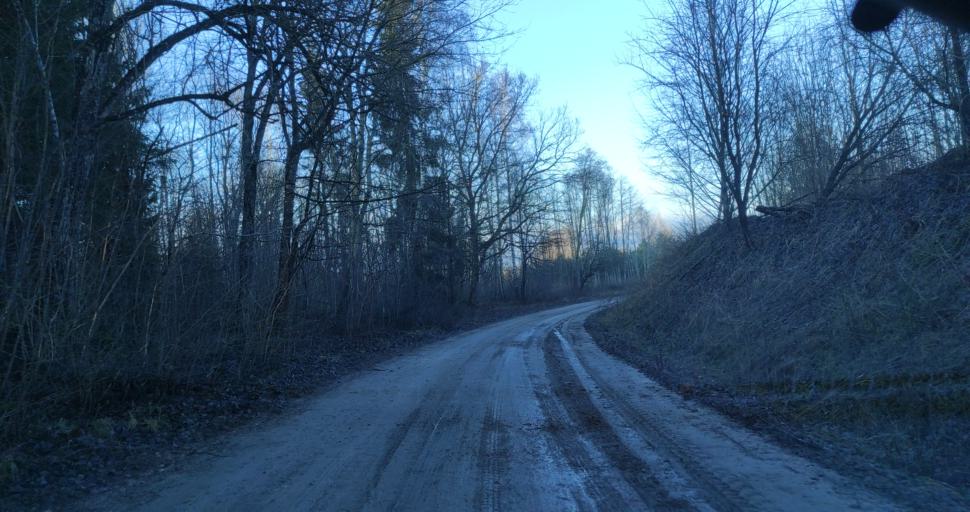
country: LV
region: Kuldigas Rajons
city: Kuldiga
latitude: 57.0469
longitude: 21.8640
